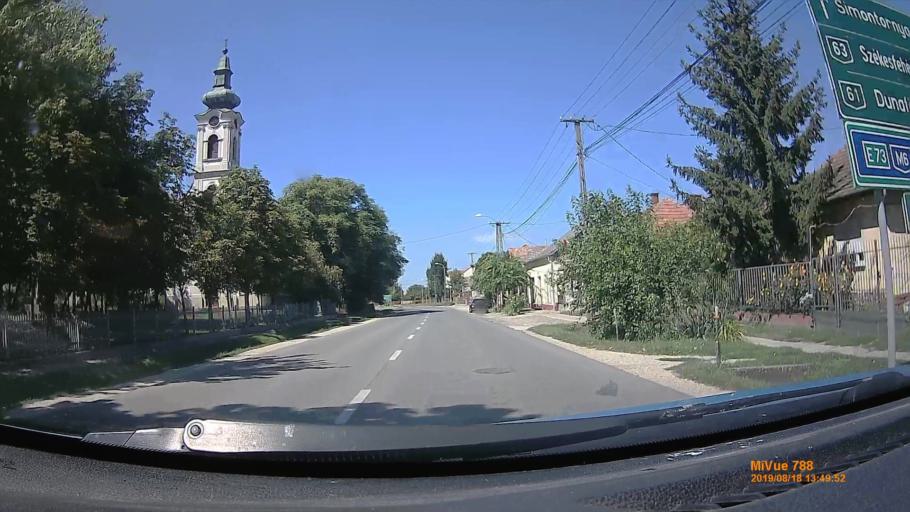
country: HU
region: Fejer
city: Cece
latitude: 46.7688
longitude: 18.6293
